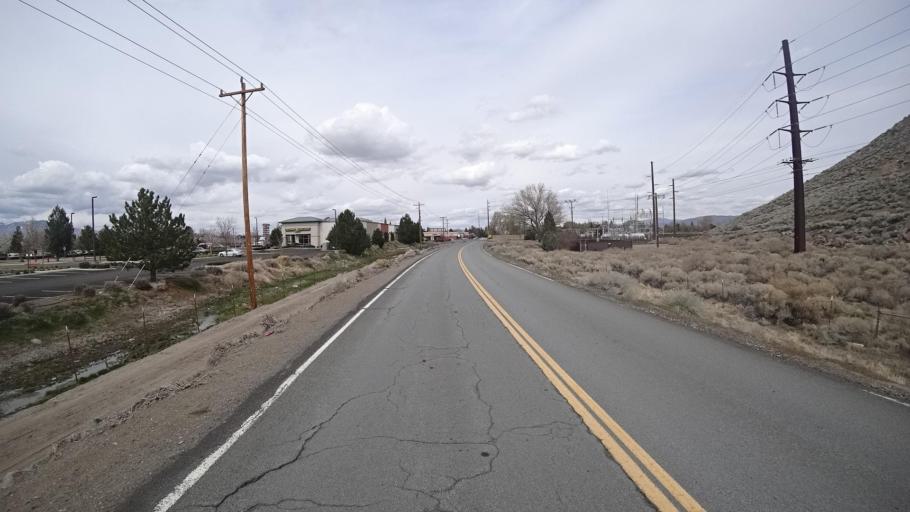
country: US
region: Nevada
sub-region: Washoe County
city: Sparks
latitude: 39.4750
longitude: -119.7632
